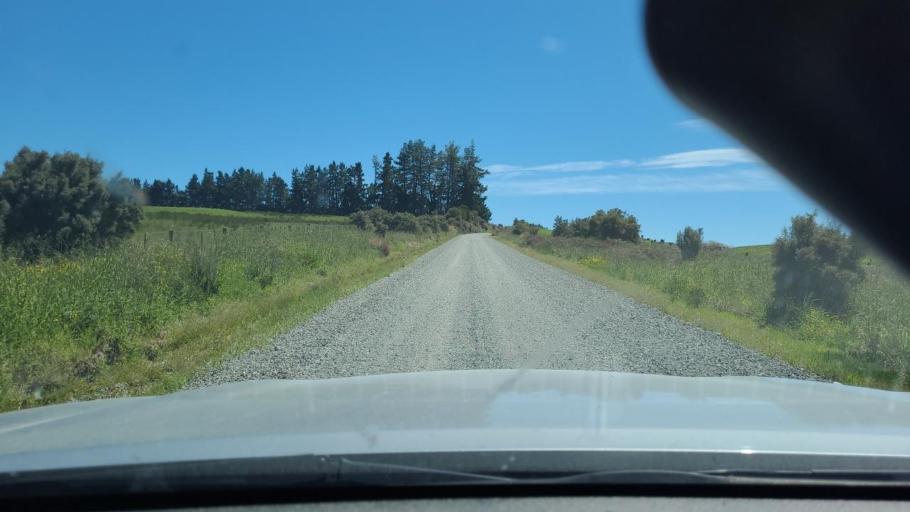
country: NZ
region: Southland
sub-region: Southland District
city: Te Anau
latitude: -45.4787
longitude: 167.8877
